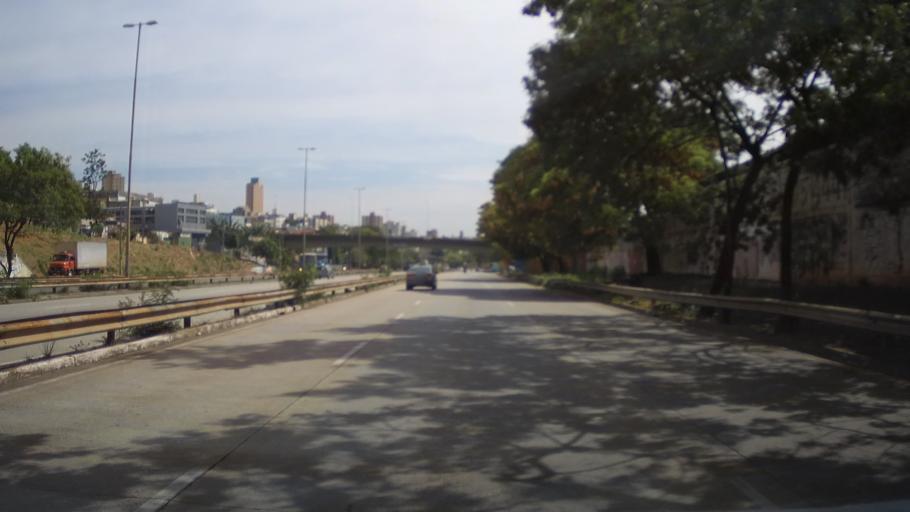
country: BR
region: Minas Gerais
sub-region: Contagem
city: Contagem
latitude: -19.9339
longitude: -43.9953
